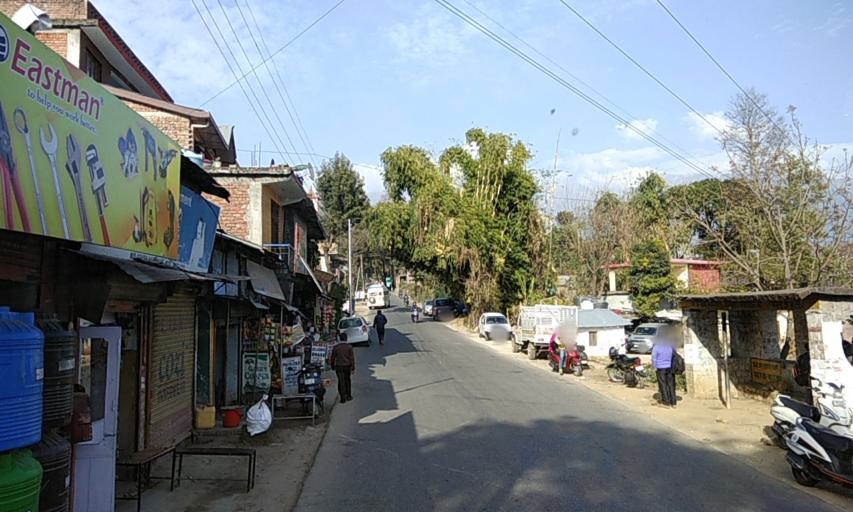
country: IN
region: Himachal Pradesh
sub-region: Kangra
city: Palampur
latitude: 32.0849
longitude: 76.5234
